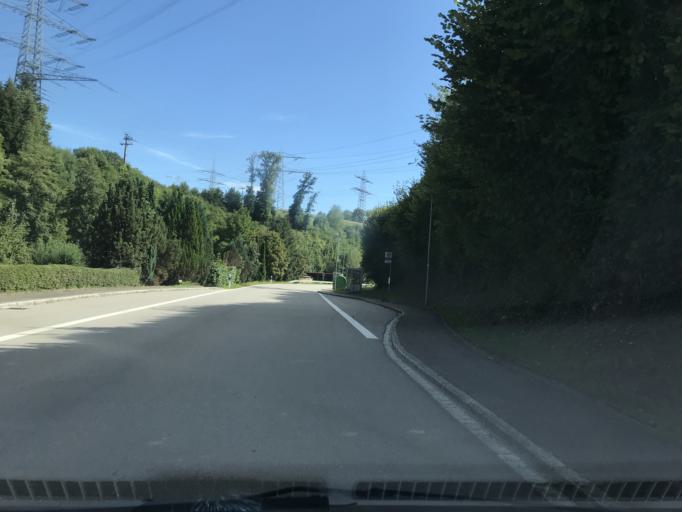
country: DE
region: Baden-Wuerttemberg
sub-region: Freiburg Region
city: Schworstadt
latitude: 47.6043
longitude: 7.8701
